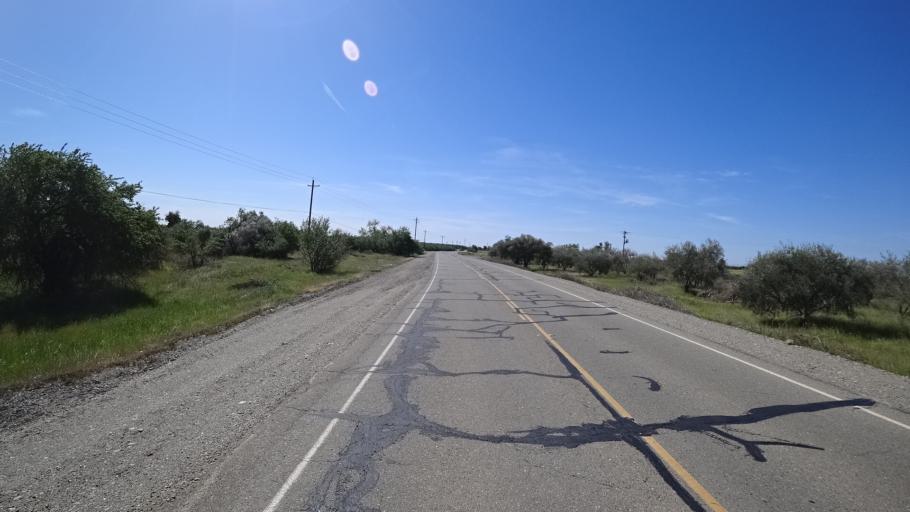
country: US
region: California
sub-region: Glenn County
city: Hamilton City
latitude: 39.7440
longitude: -122.1046
